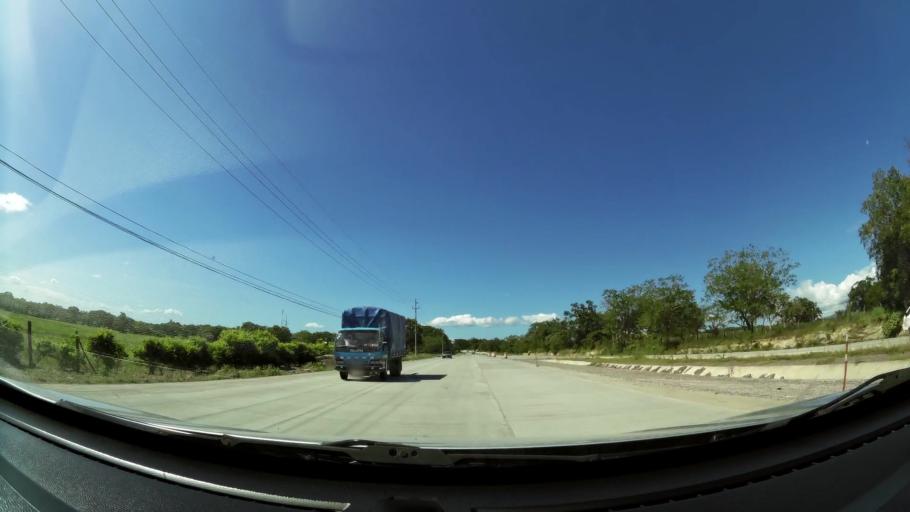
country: CR
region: Guanacaste
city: Liberia
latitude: 10.5580
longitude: -85.3772
